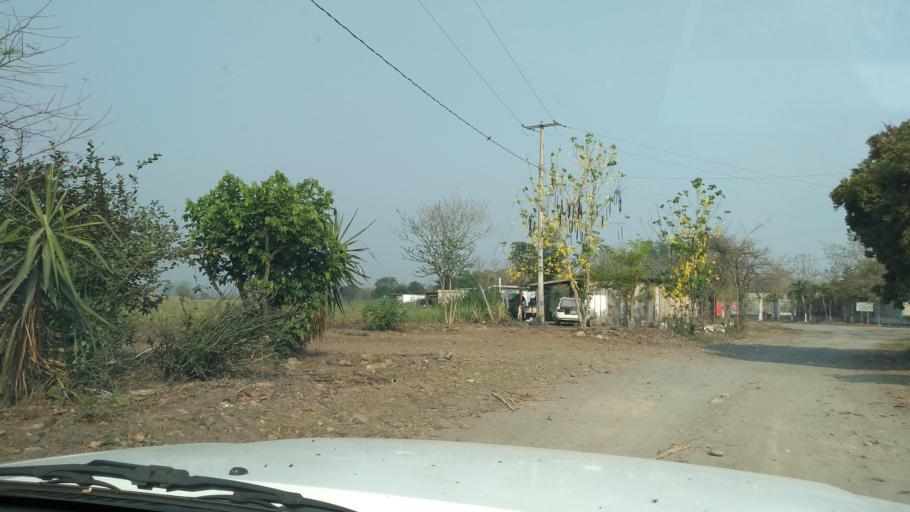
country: MX
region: Oaxaca
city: Acatlan de Perez Figueroa
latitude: 18.6222
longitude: -96.6008
